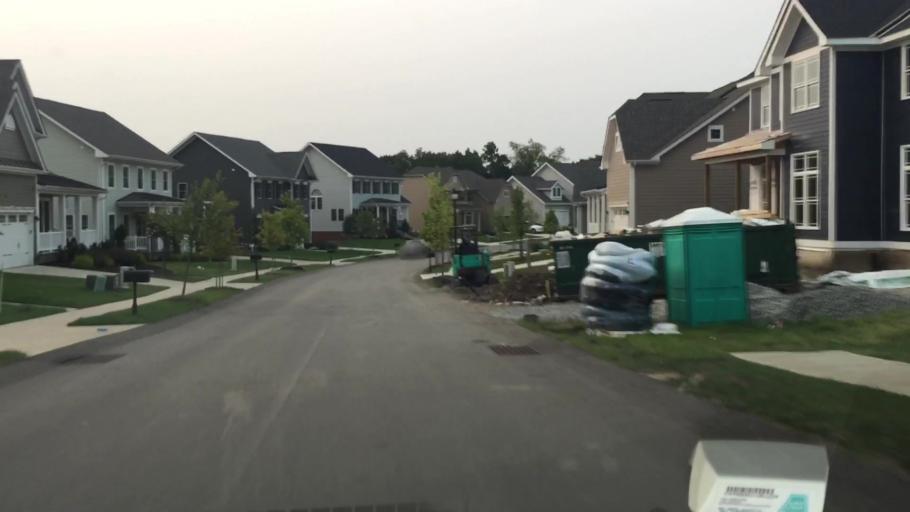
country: US
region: Pennsylvania
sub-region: Butler County
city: Cranberry Township
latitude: 40.6657
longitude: -80.0906
